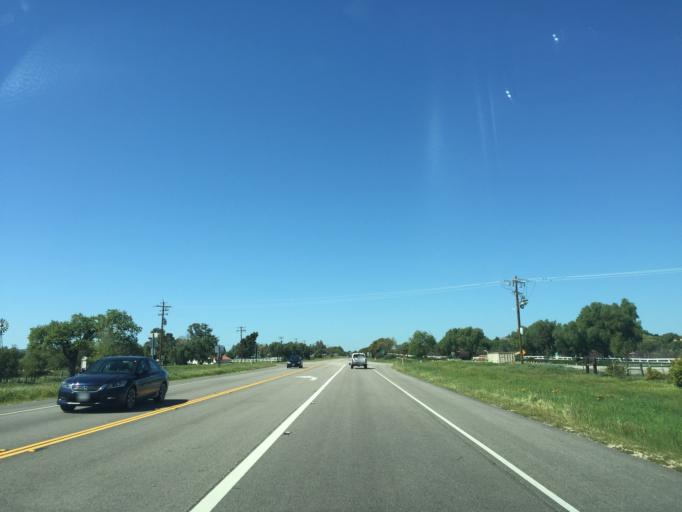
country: US
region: California
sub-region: Santa Barbara County
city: Los Olivos
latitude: 34.6497
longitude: -120.0946
